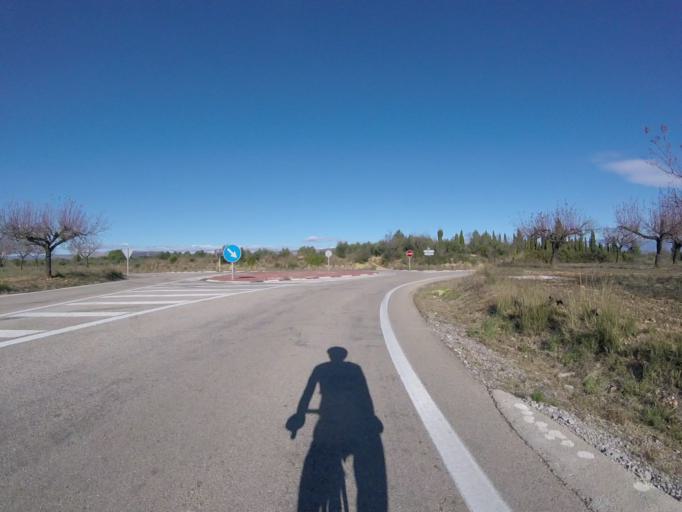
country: ES
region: Valencia
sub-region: Provincia de Castello
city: Cervera del Maestre
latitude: 40.4773
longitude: 0.2172
